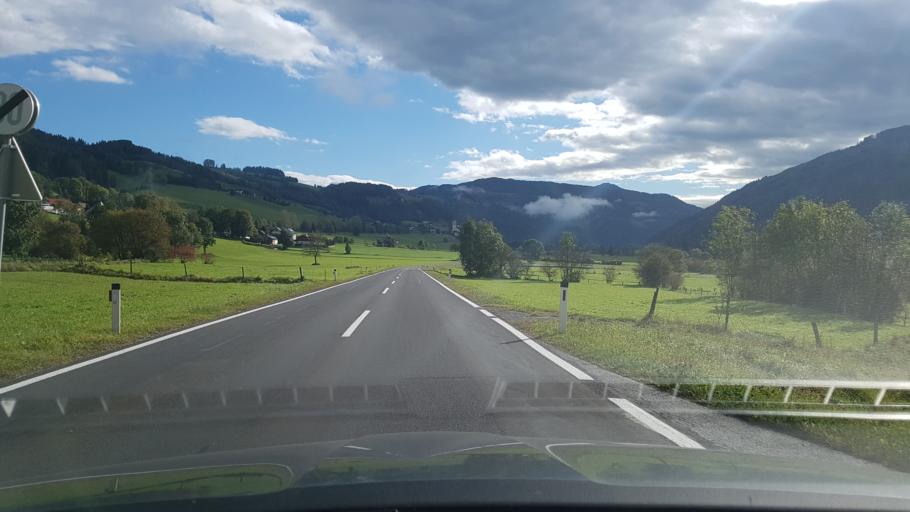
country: AT
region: Styria
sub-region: Politischer Bezirk Murau
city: Sankt Peter am Kammersberg
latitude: 47.1879
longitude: 14.1636
